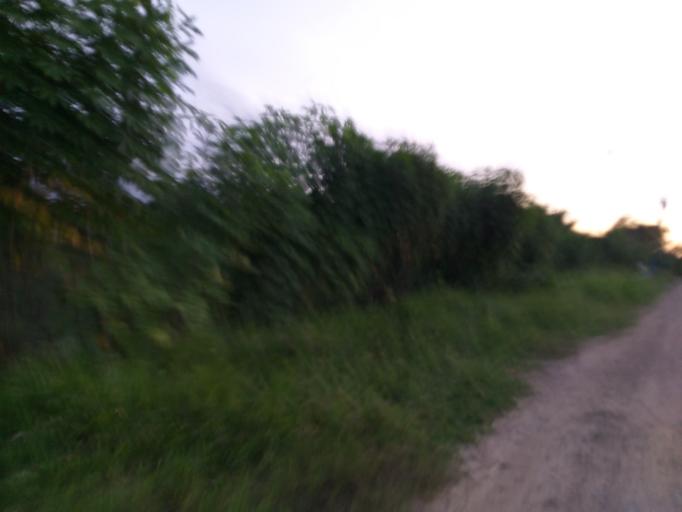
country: TH
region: Pathum Thani
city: Ban Rangsit
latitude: 14.0262
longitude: 100.8015
